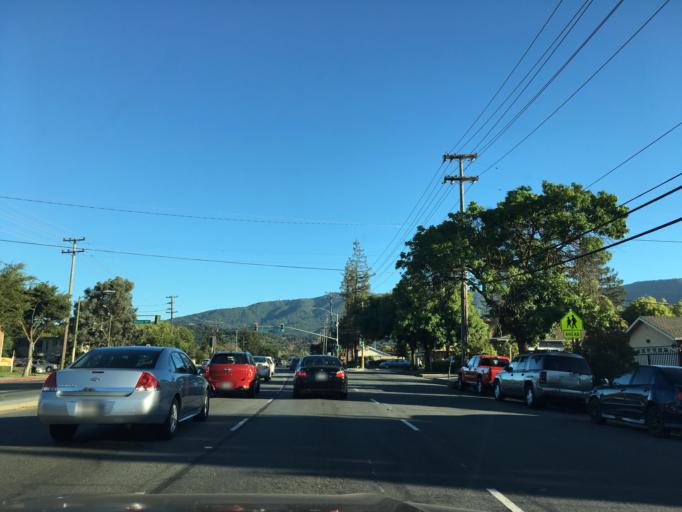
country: US
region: California
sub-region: Santa Clara County
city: Cambrian Park
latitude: 37.2372
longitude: -121.9037
